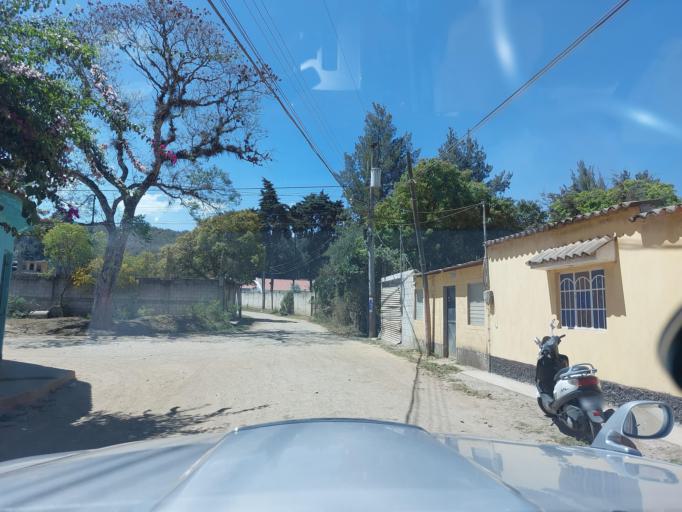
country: GT
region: Chimaltenango
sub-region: Municipio de Chimaltenango
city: Chimaltenango
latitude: 14.6546
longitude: -90.8271
